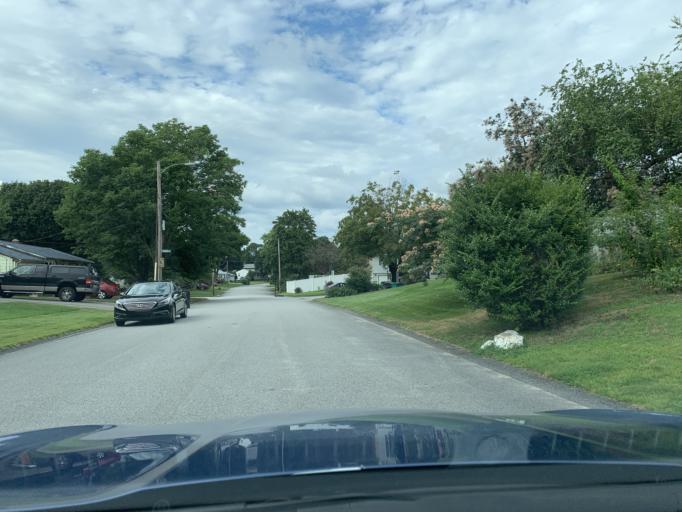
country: US
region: Rhode Island
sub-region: Kent County
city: East Greenwich
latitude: 41.6410
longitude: -71.4591
